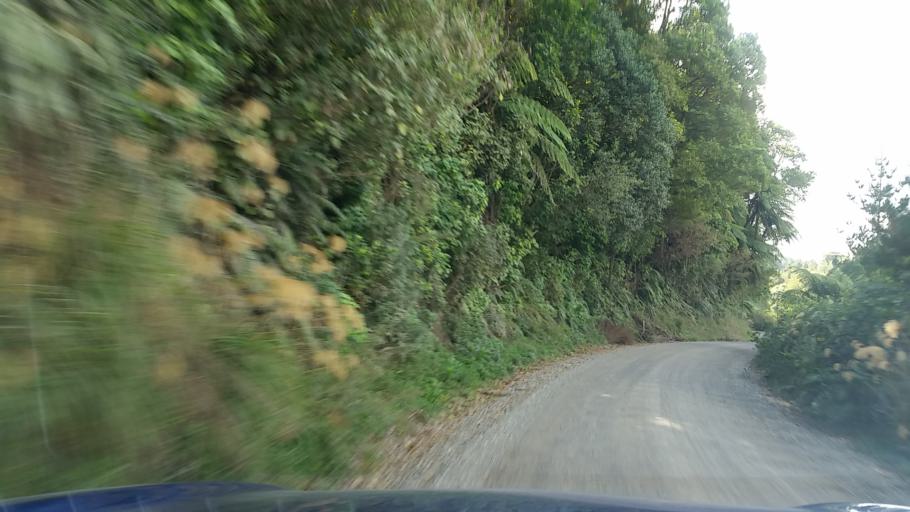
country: NZ
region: Bay of Plenty
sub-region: Western Bay of Plenty District
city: Maketu
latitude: -37.9602
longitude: 176.4375
